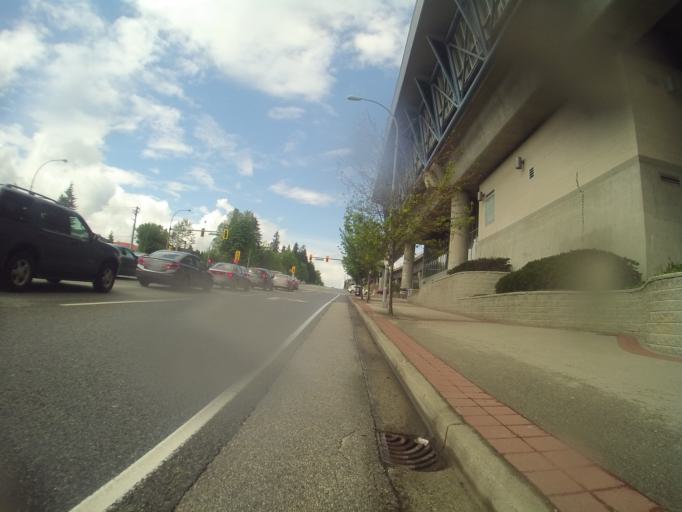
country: CA
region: British Columbia
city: Burnaby
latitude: 49.2533
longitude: -122.9178
